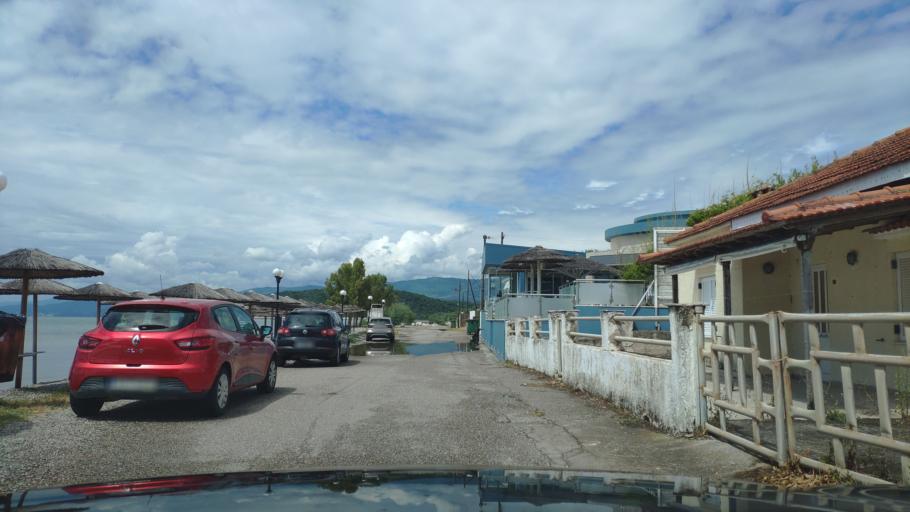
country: GR
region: West Greece
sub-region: Nomos Aitolias kai Akarnanias
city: Krikellos
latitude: 38.9287
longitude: 21.1407
